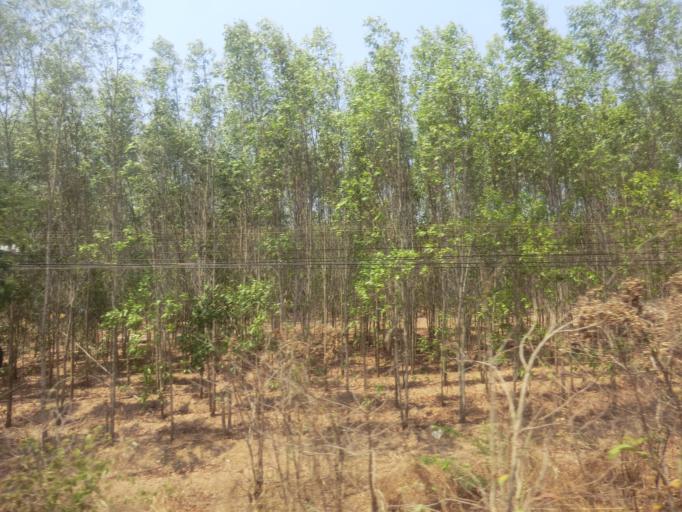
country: VN
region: Binh Thuan
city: Thuan Nam
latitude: 10.9283
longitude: 107.9101
